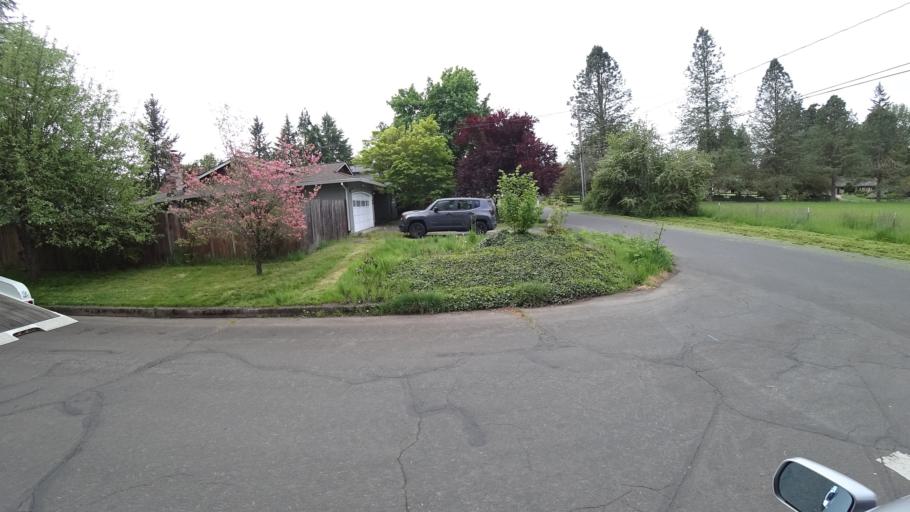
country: US
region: Oregon
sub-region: Washington County
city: Hillsboro
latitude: 45.5322
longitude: -123.0003
